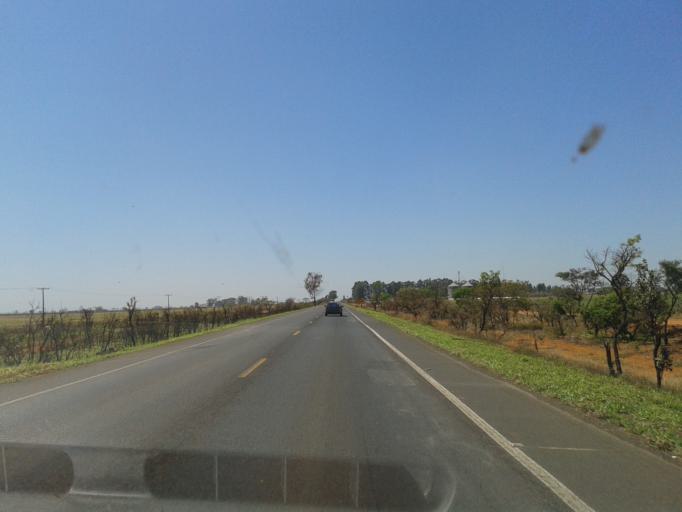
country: BR
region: Minas Gerais
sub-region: Uberaba
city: Uberaba
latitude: -19.3068
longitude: -47.5819
